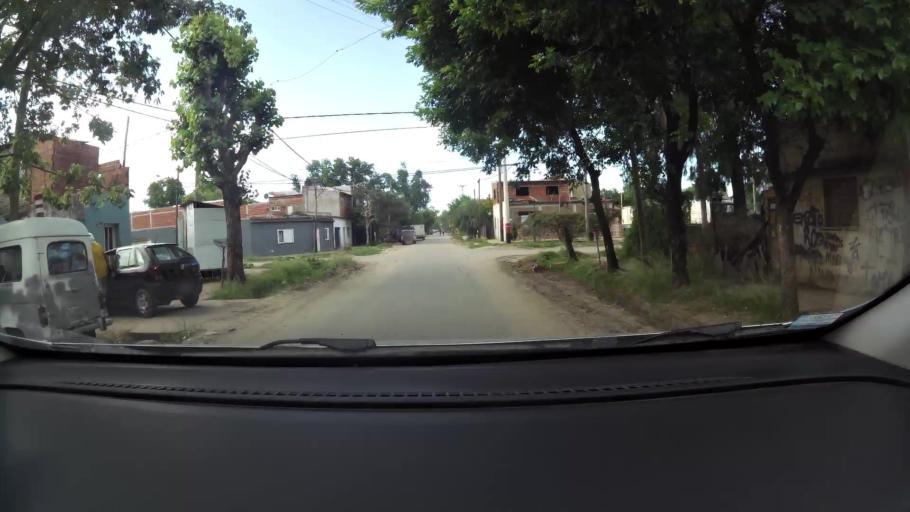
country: AR
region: Santa Fe
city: Granadero Baigorria
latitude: -32.9149
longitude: -60.7063
